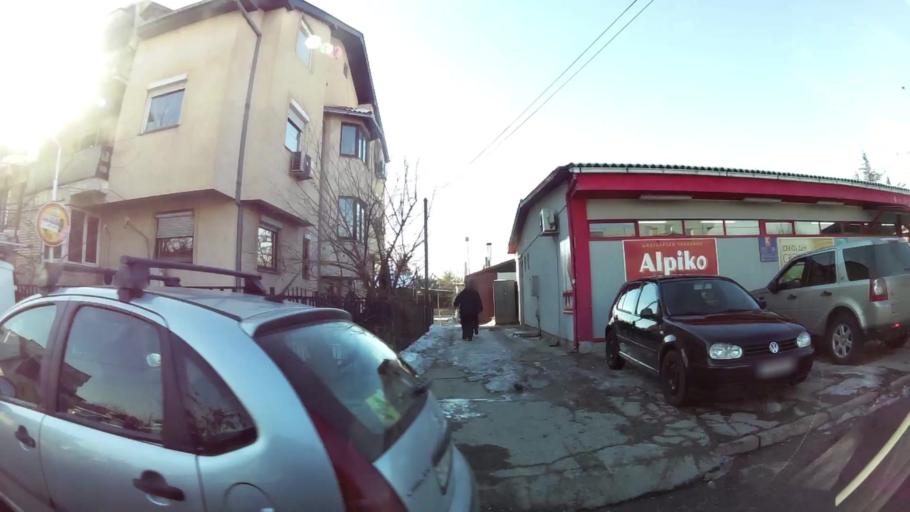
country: MK
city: Krushopek
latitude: 42.0103
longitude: 21.3745
